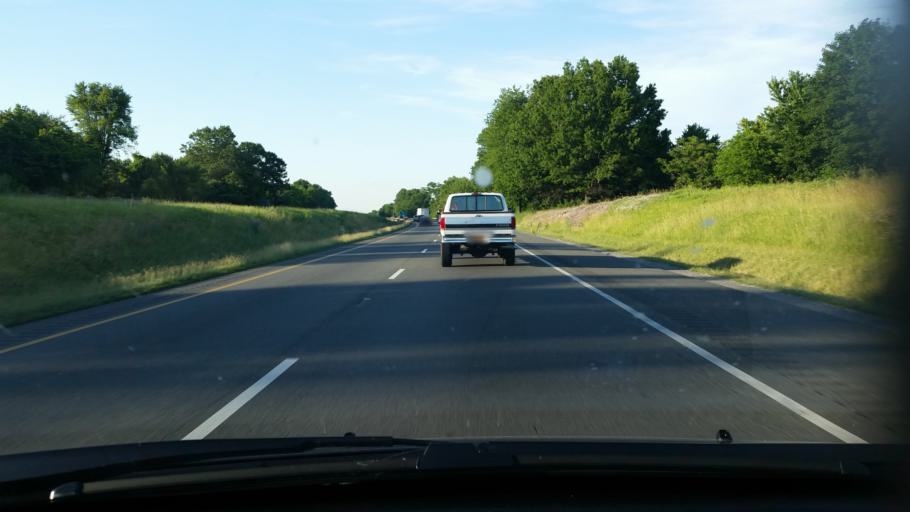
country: US
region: Maryland
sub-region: Washington County
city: Williamsport
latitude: 39.5921
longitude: -77.8104
